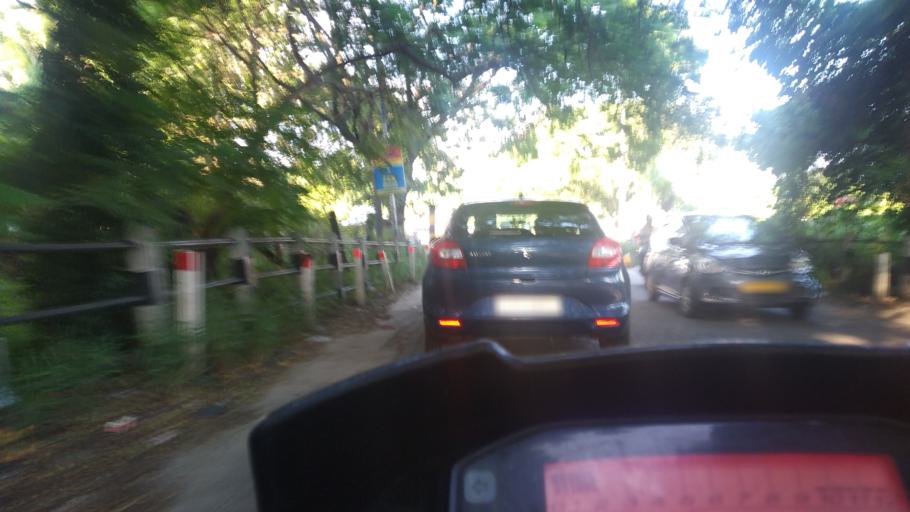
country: IN
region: Kerala
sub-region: Ernakulam
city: Cochin
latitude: 9.9383
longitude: 76.2687
